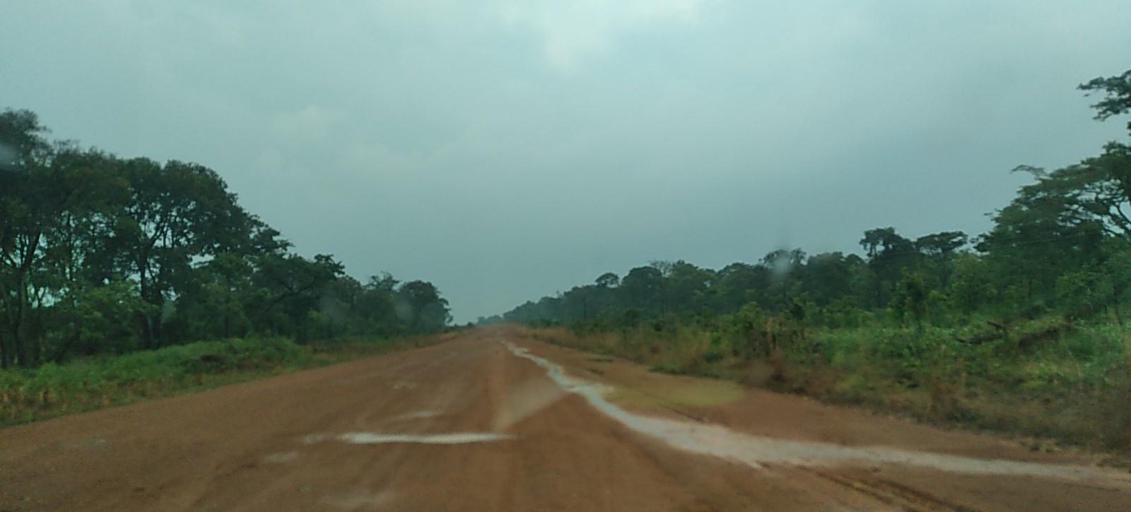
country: ZM
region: North-Western
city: Mwinilunga
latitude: -11.6010
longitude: 24.3936
